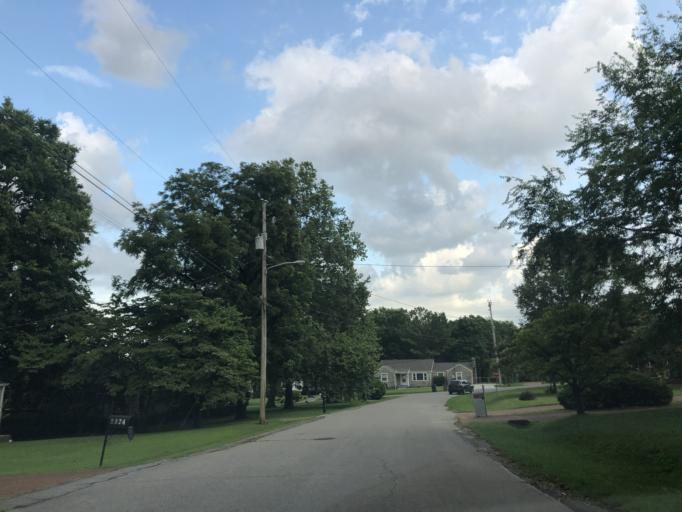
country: US
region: Tennessee
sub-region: Davidson County
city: Lakewood
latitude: 36.1789
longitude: -86.6844
